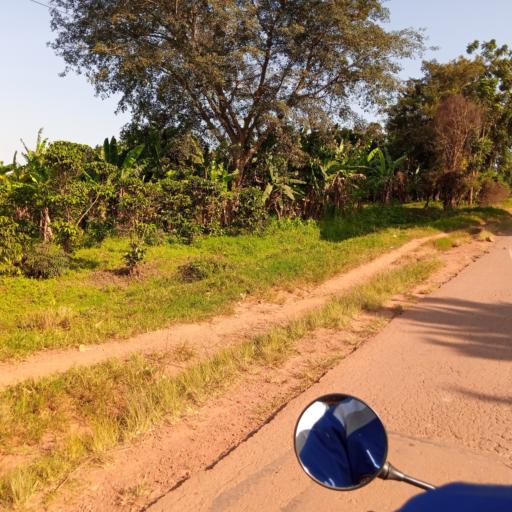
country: UG
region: Central Region
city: Masaka
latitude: -0.4398
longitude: 31.6640
